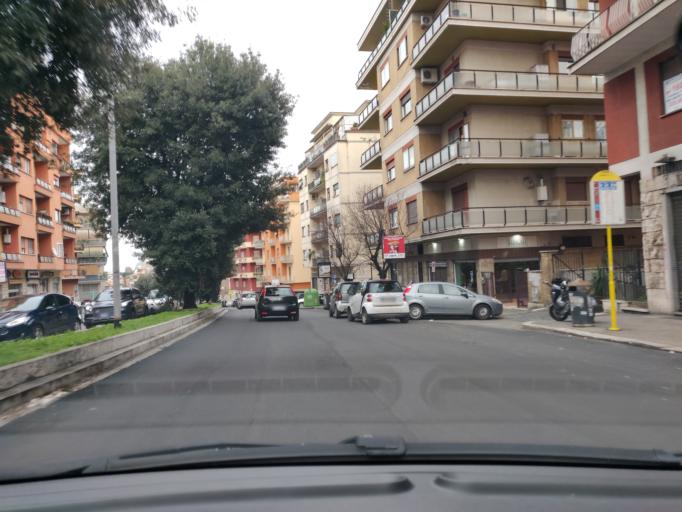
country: VA
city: Vatican City
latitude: 41.8984
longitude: 12.4304
